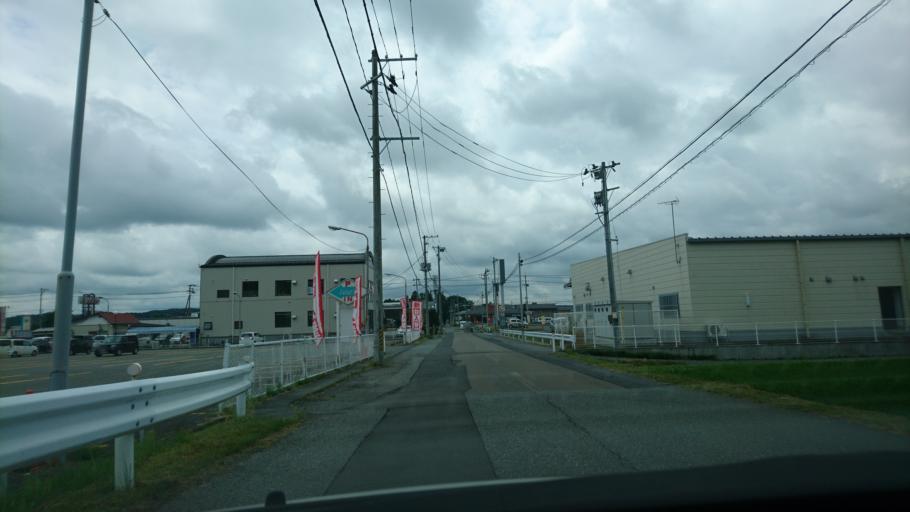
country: JP
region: Iwate
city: Ichinoseki
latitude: 38.9397
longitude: 141.1087
